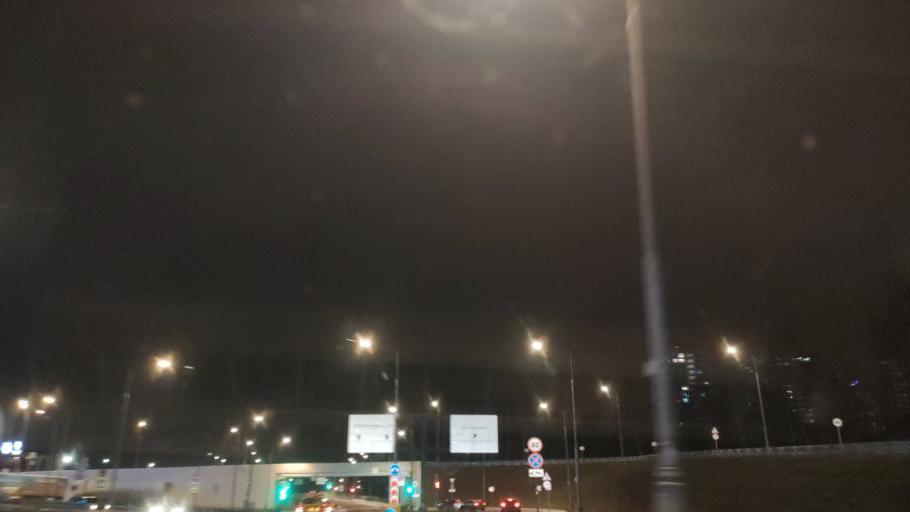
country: RU
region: Moscow
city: Solntsevo
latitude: 55.6230
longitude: 37.4193
